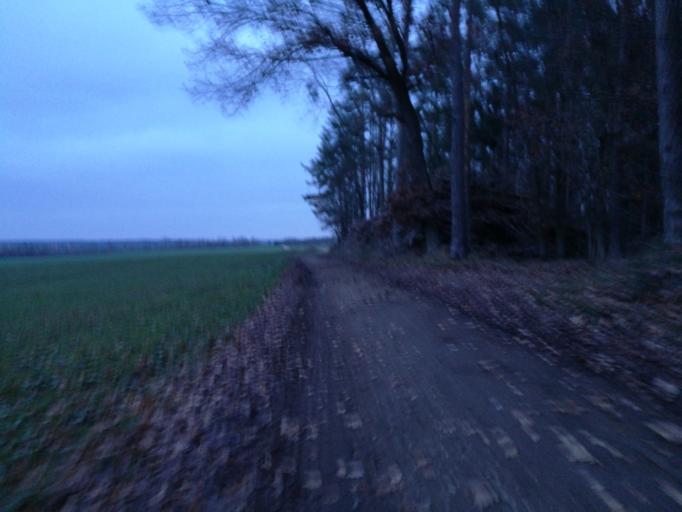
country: DE
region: Bavaria
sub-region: Regierungsbezirk Mittelfranken
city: Seukendorf
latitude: 49.4747
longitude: 10.8857
